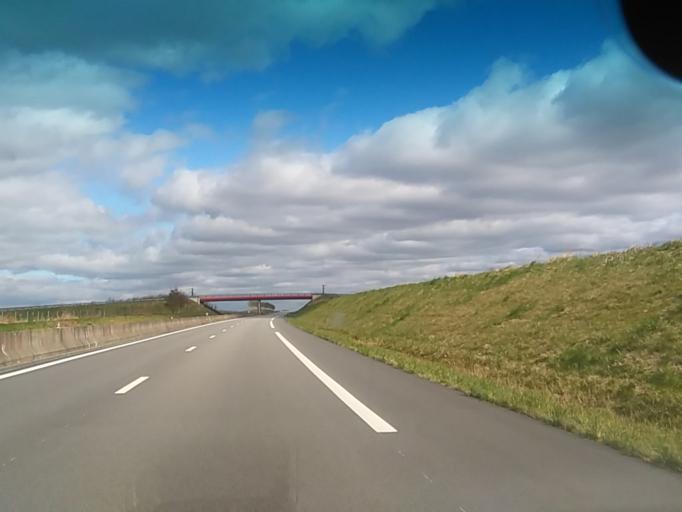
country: FR
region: Haute-Normandie
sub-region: Departement de l'Eure
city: Bourg-Achard
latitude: 49.3006
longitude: 0.7965
